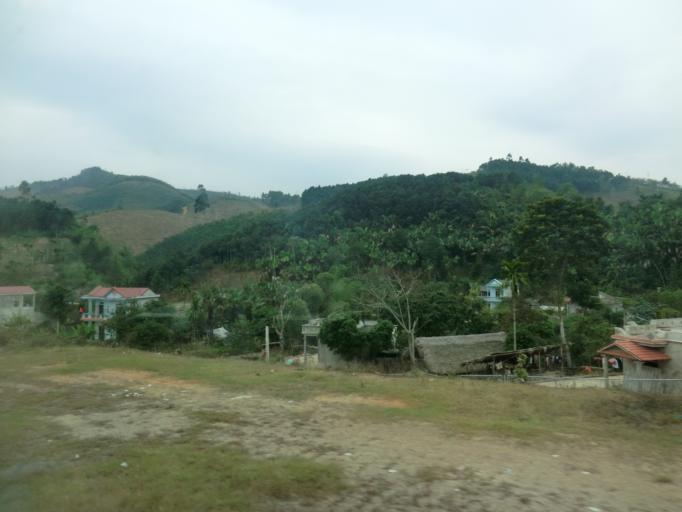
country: VN
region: Yen Bai
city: Thi Tran Yen The
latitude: 21.9264
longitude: 104.5992
